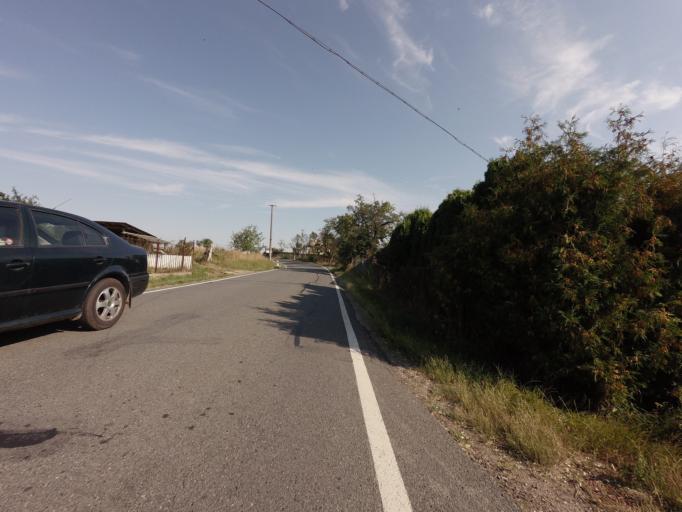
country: CZ
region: Jihocesky
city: Bernartice
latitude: 49.3059
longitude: 14.3802
